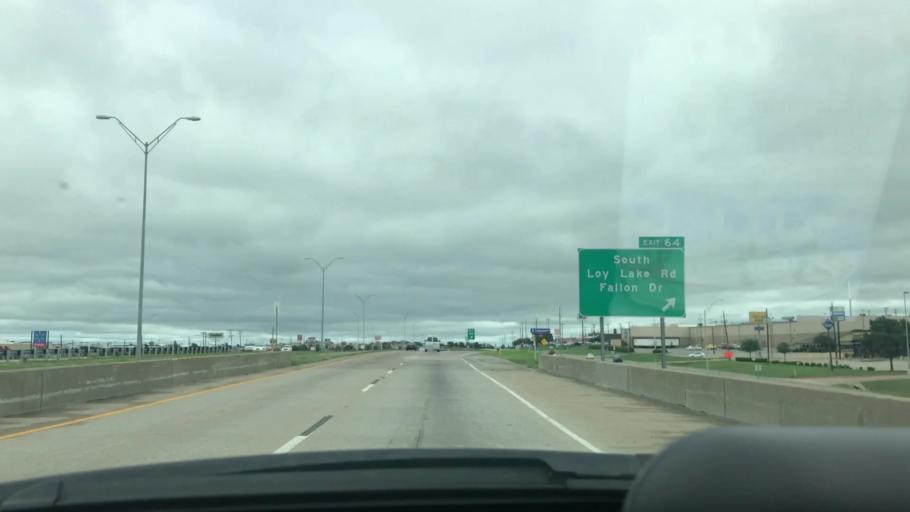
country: US
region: Texas
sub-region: Grayson County
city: Sherman
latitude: 33.6710
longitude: -96.6098
